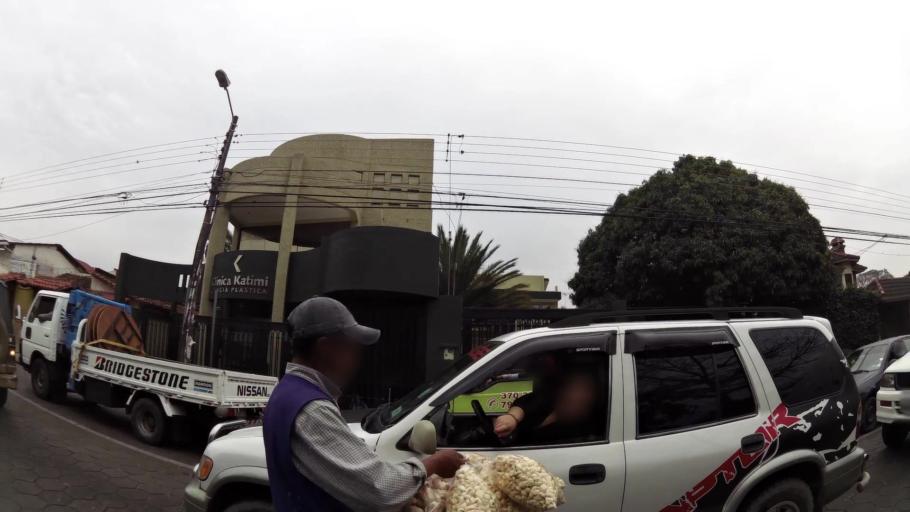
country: BO
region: Santa Cruz
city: Santa Cruz de la Sierra
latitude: -17.7987
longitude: -63.1805
